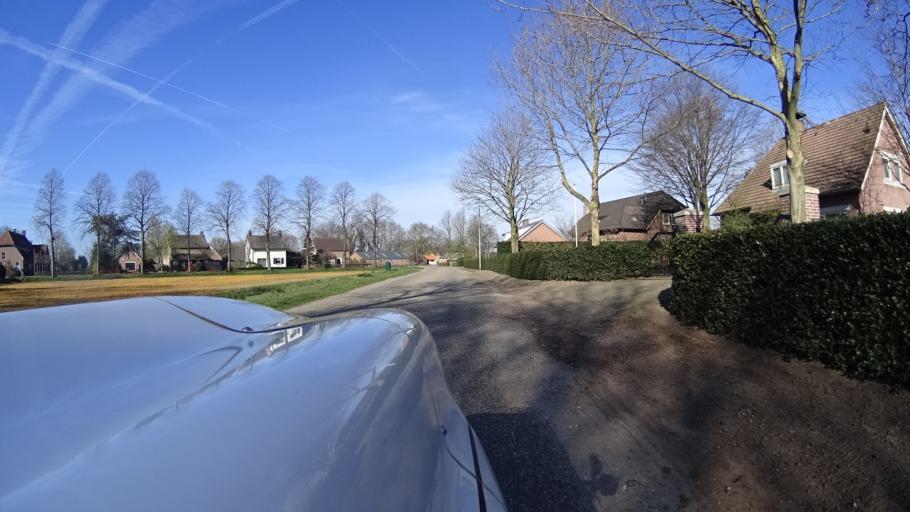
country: NL
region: North Brabant
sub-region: Gemeente Uden
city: Volkel
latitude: 51.6427
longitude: 5.6712
